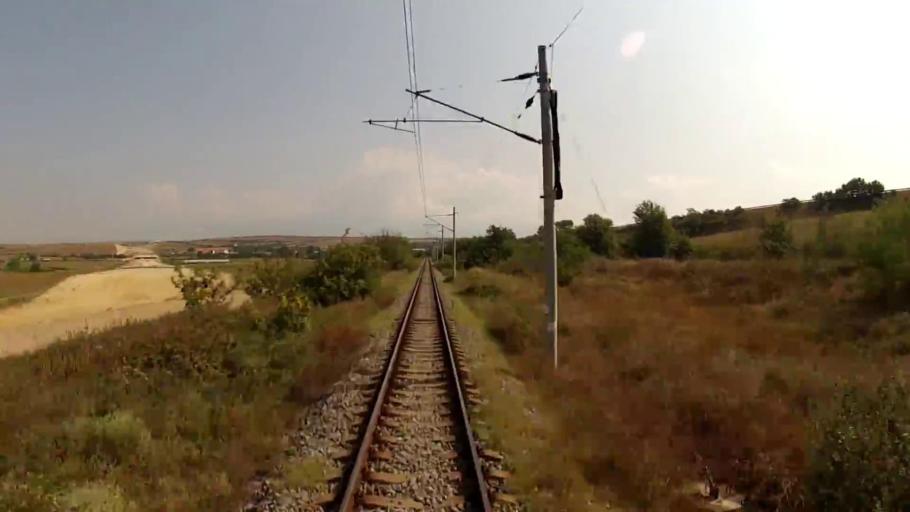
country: BG
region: Blagoevgrad
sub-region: Obshtina Petrich
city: Petrich
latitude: 41.4362
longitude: 23.3310
